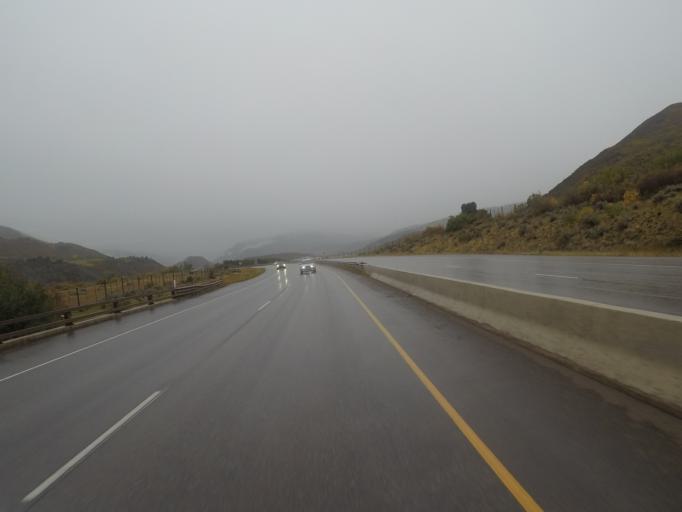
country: US
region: Colorado
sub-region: Pitkin County
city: Snowmass Village
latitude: 39.2382
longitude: -106.8765
